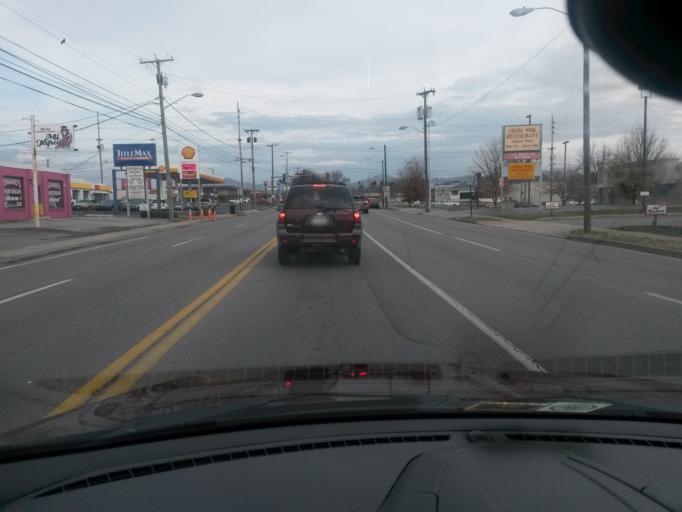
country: US
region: Virginia
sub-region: Roanoke County
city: Hollins
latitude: 37.3155
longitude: -79.9544
